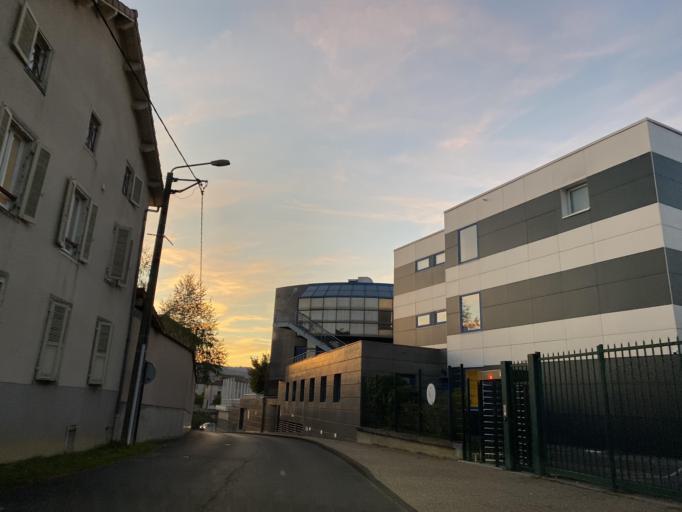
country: FR
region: Auvergne
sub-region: Departement du Puy-de-Dome
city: Ambert
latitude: 45.5450
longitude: 3.7472
